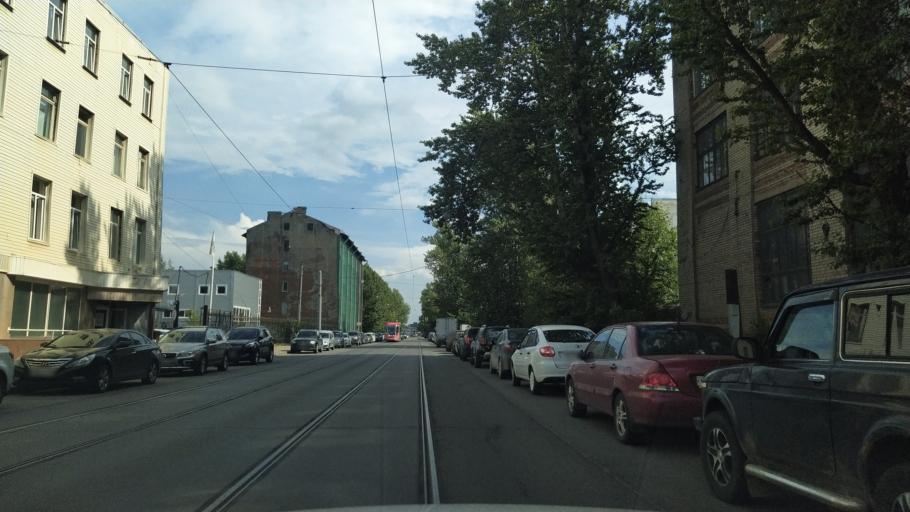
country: RU
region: Leningrad
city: Finlyandskiy
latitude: 59.9662
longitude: 30.3888
